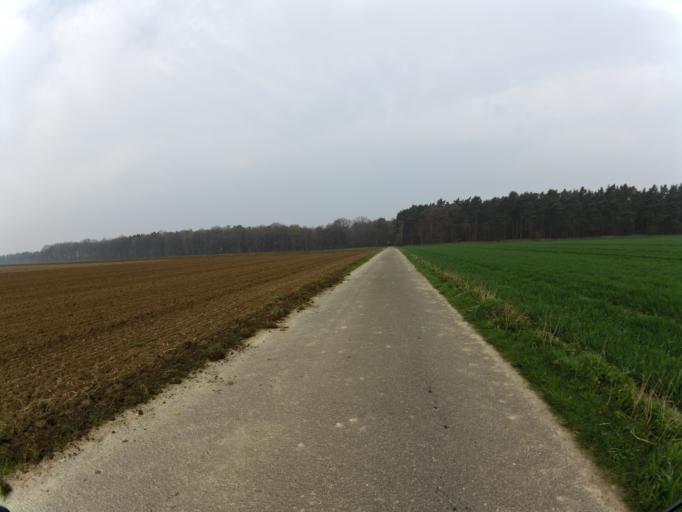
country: DE
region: North Rhine-Westphalia
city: Geilenkirchen
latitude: 50.9732
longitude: 6.0633
